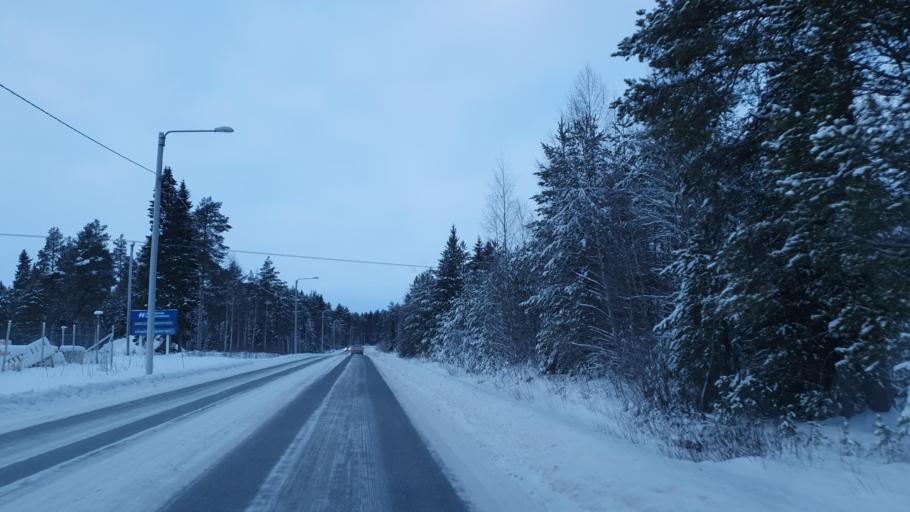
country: FI
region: Northern Ostrobothnia
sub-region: Oulu
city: Haukipudas
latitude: 65.1924
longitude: 25.3596
